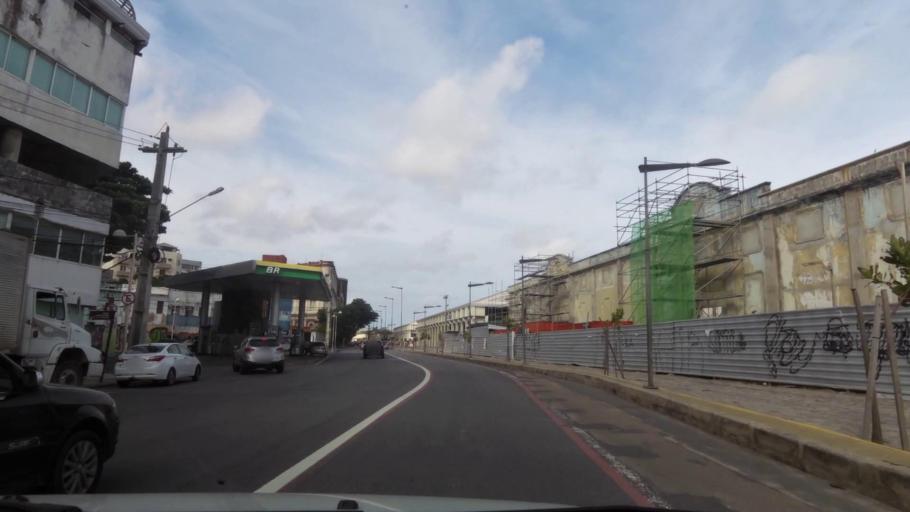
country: BR
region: Pernambuco
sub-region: Recife
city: Recife
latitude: -8.0640
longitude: -34.8717
